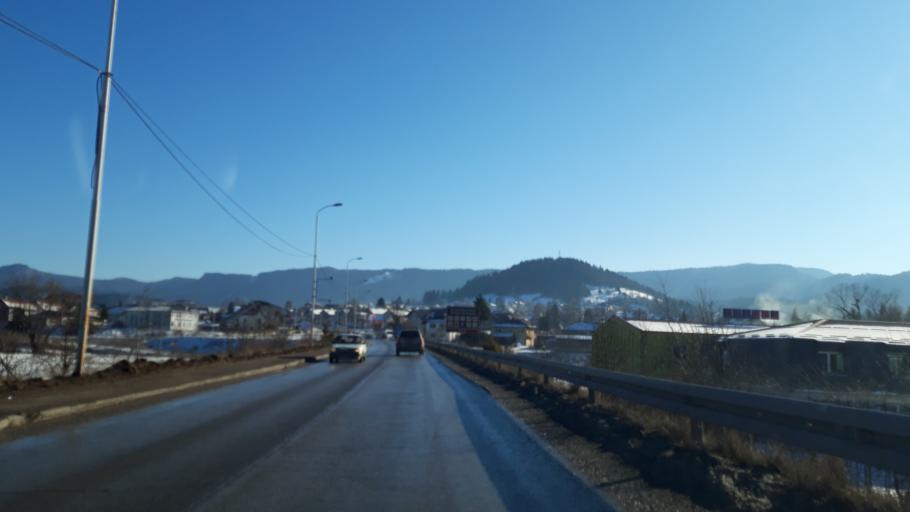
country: BA
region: Republika Srpska
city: Pale
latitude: 43.8181
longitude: 18.5597
